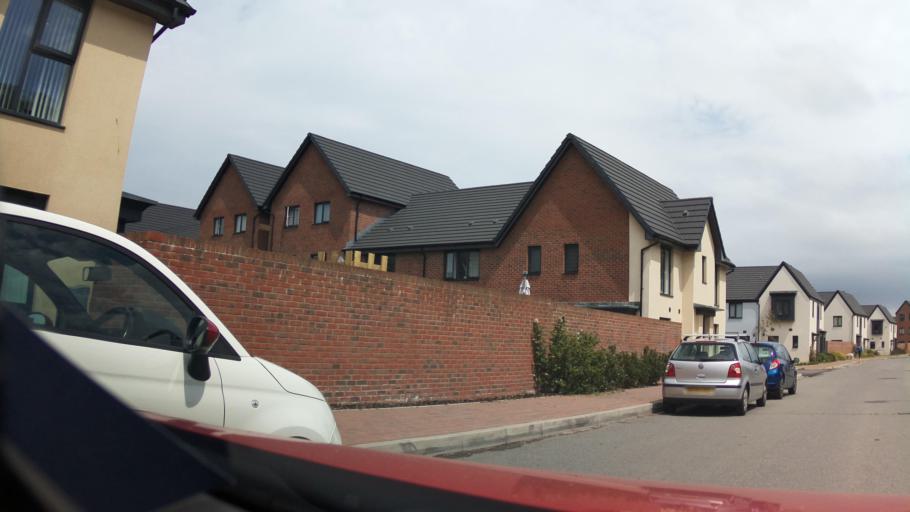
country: GB
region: Wales
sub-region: Vale of Glamorgan
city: Barry
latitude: 51.3949
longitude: -3.2764
